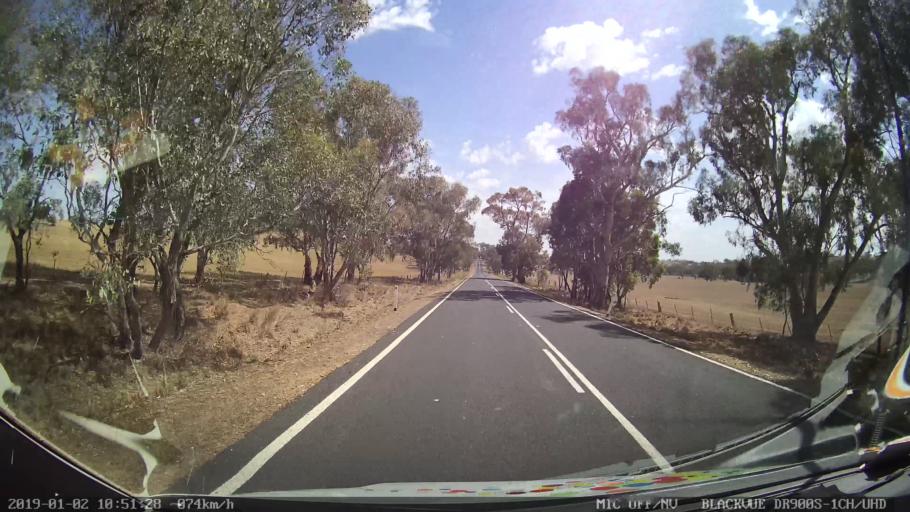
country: AU
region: New South Wales
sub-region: Cootamundra
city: Cootamundra
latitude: -34.6999
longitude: 148.2758
